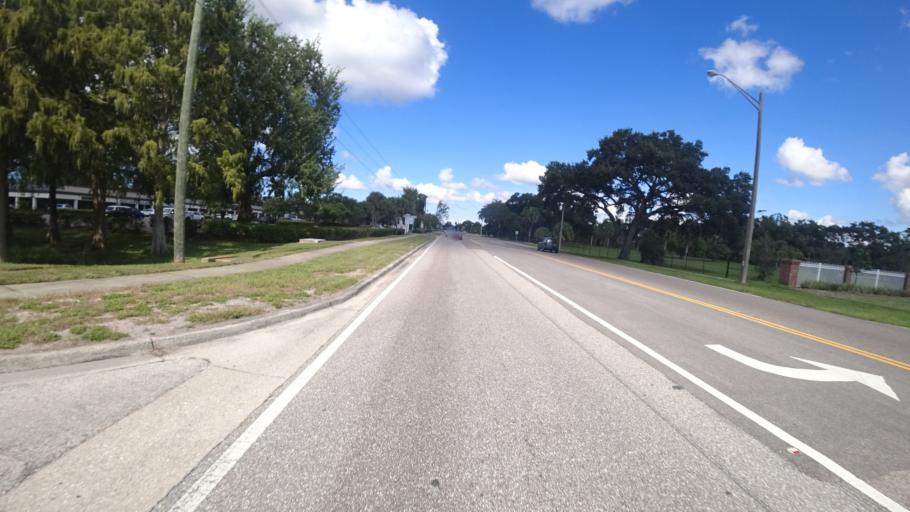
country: US
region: Florida
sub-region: Manatee County
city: West Bradenton
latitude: 27.4830
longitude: -82.6205
